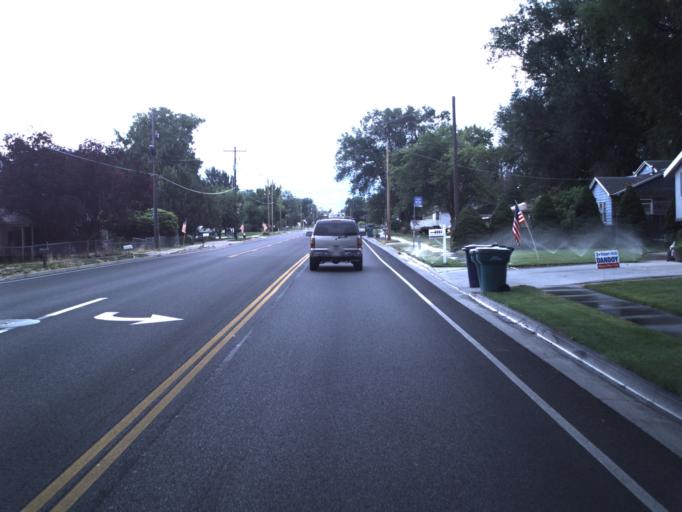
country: US
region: Utah
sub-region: Davis County
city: Clinton
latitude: 41.1616
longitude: -112.0546
